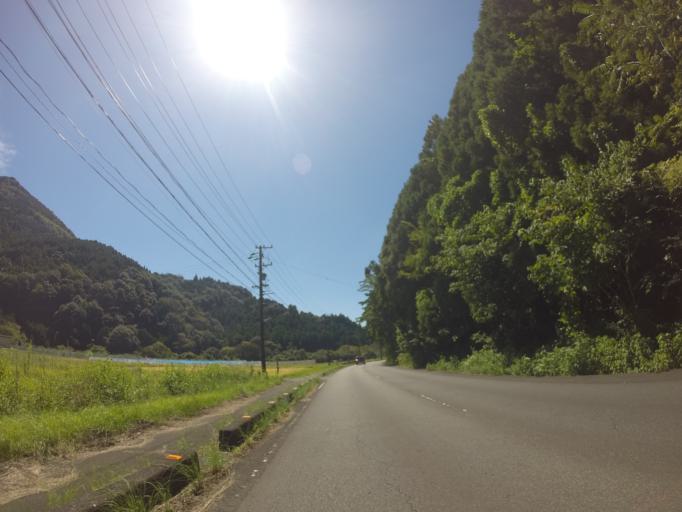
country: JP
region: Shizuoka
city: Fujieda
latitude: 34.9514
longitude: 138.2119
